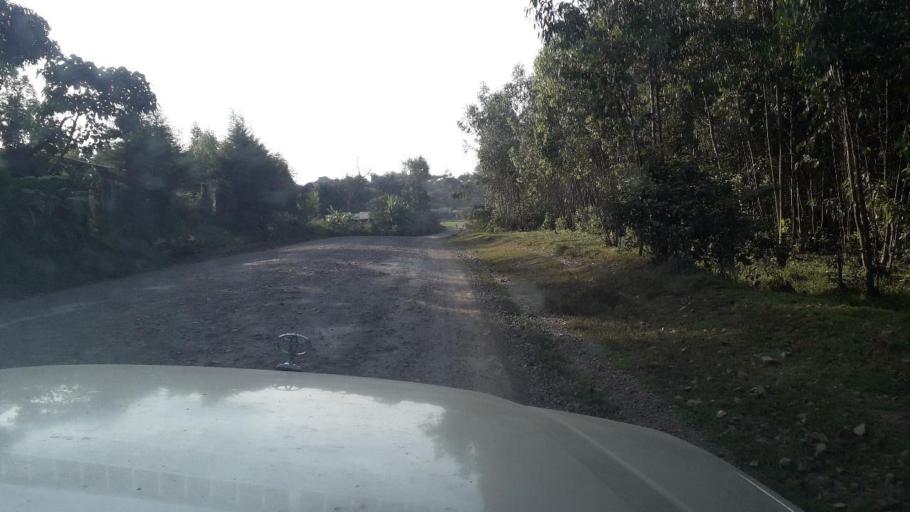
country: ET
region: Oromiya
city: Jima
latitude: 7.5953
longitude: 36.8494
